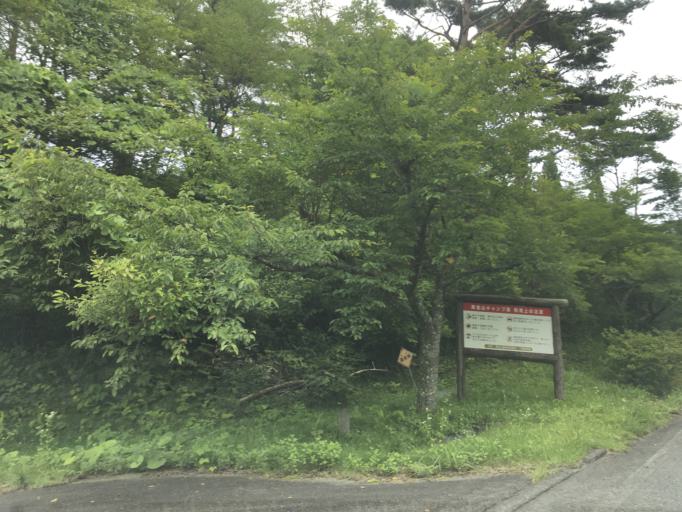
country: JP
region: Iwate
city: Ichinoseki
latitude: 38.8682
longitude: 141.3994
